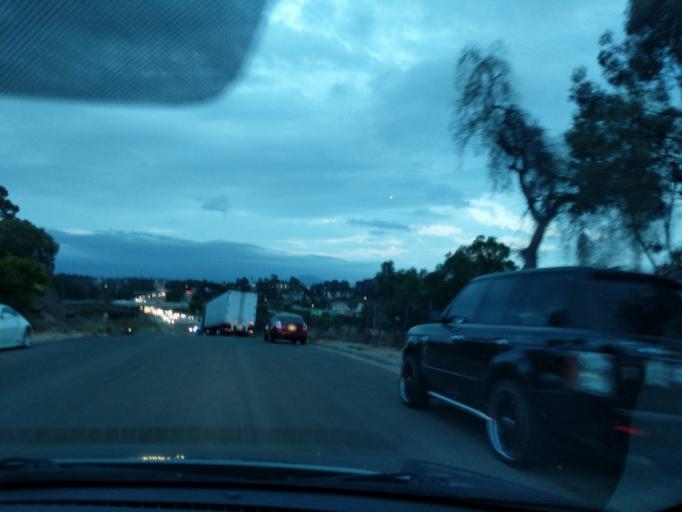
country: US
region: California
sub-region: San Diego County
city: San Diego
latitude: 32.7170
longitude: -117.1209
